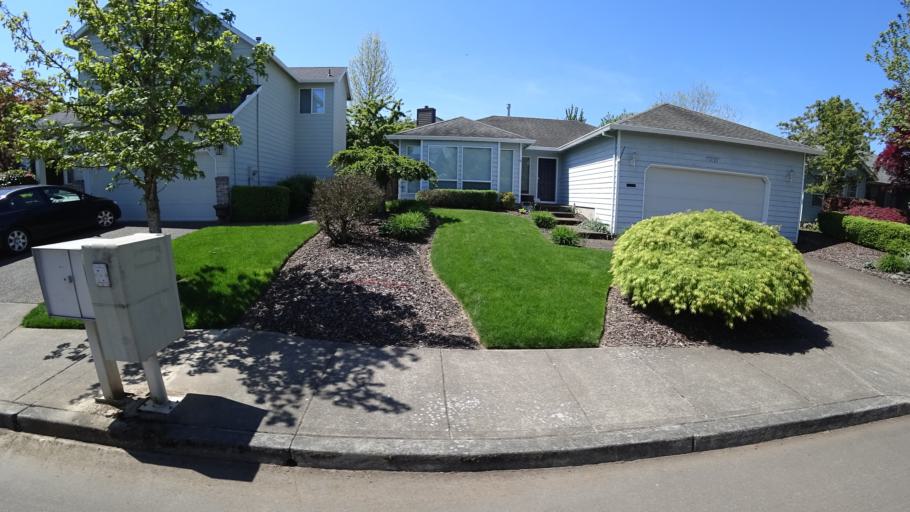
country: US
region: Oregon
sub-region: Washington County
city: King City
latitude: 45.4302
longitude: -122.8230
